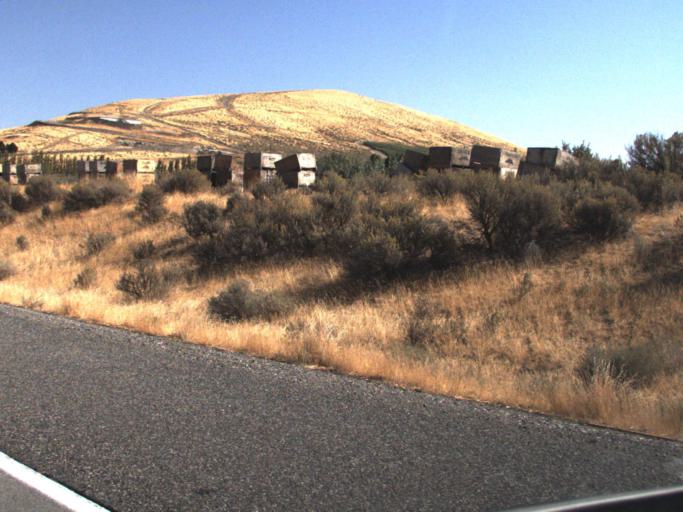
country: US
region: Washington
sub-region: Benton County
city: West Richland
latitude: 46.2452
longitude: -119.3490
